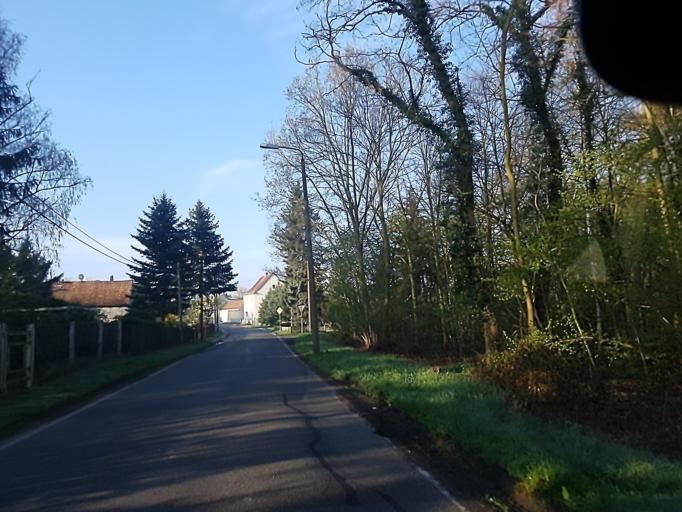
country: DE
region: Saxony
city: Cavertitz
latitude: 51.4260
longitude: 13.1548
